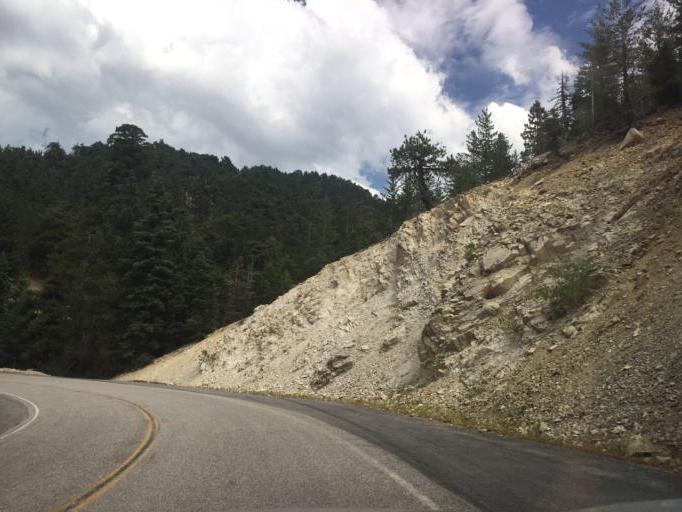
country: US
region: California
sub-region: Los Angeles County
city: Littlerock
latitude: 34.3436
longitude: -117.9098
